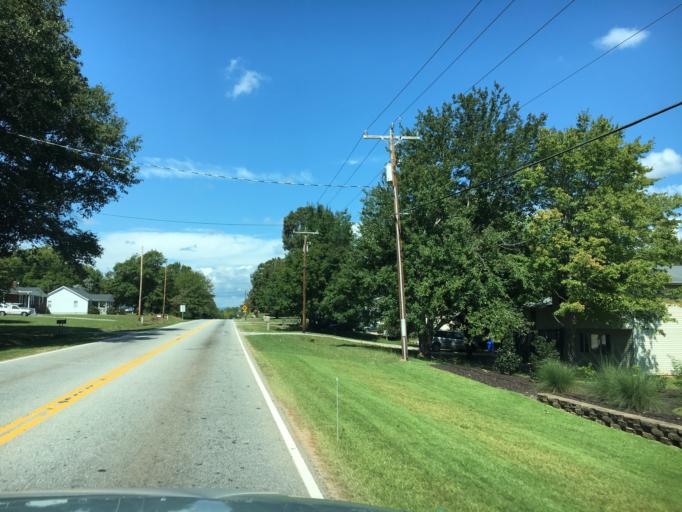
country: US
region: South Carolina
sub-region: Greenville County
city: Taylors
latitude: 34.9697
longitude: -82.3237
